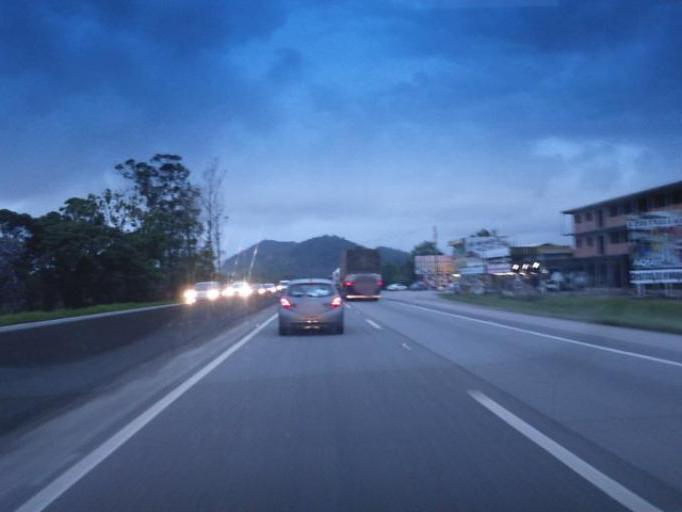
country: BR
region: Santa Catarina
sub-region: Barra Velha
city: Barra Velha
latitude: -26.5590
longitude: -48.7207
